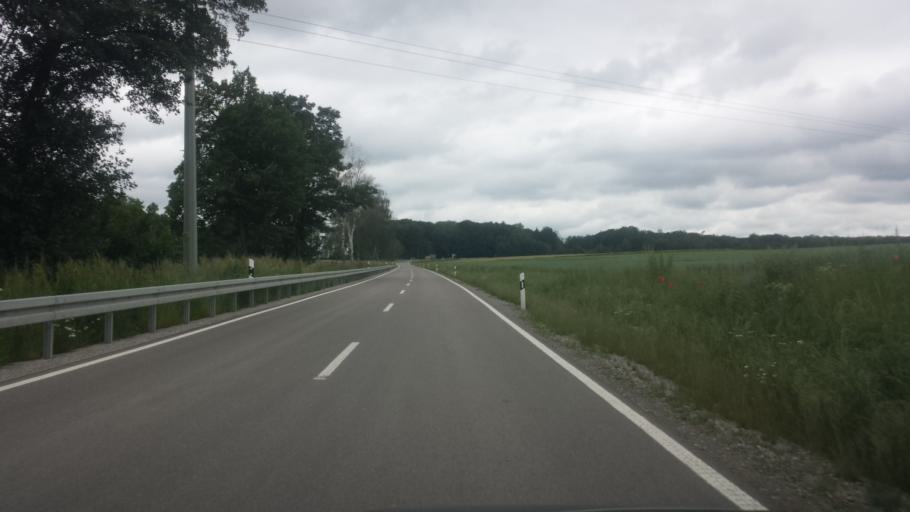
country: DE
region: Baden-Wuerttemberg
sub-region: Regierungsbezirk Stuttgart
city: Rot am See
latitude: 49.2781
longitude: 10.0168
